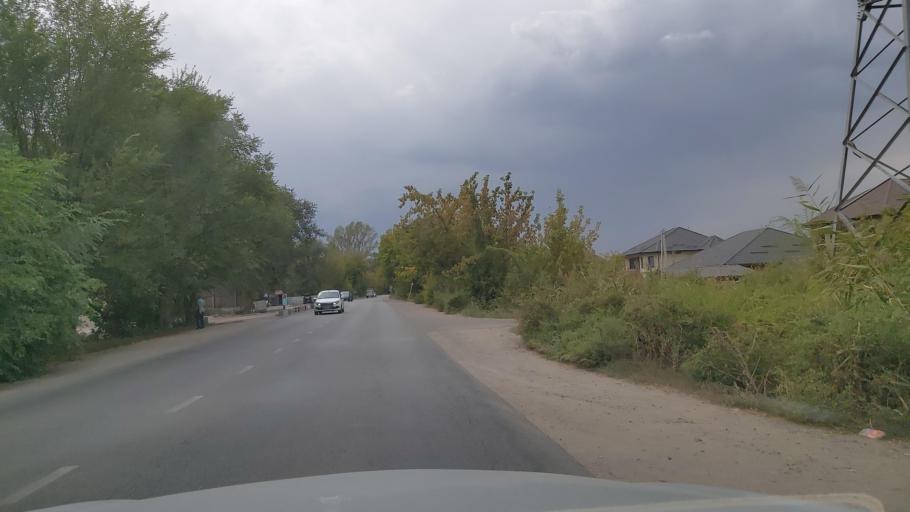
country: KZ
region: Almaty Oblysy
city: Energeticheskiy
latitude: 43.4033
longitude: 77.0300
